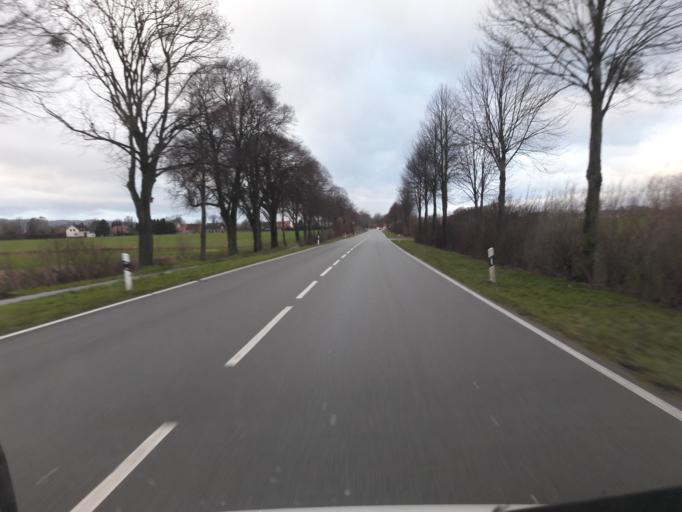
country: DE
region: North Rhine-Westphalia
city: Bad Oeynhausen
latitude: 52.2812
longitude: 8.8124
